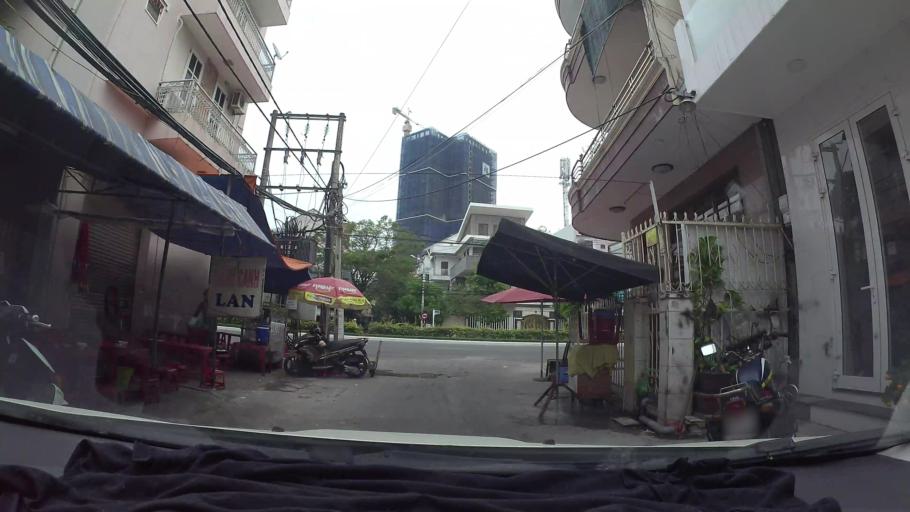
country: VN
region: Da Nang
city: Da Nang
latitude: 16.0848
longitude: 108.2201
